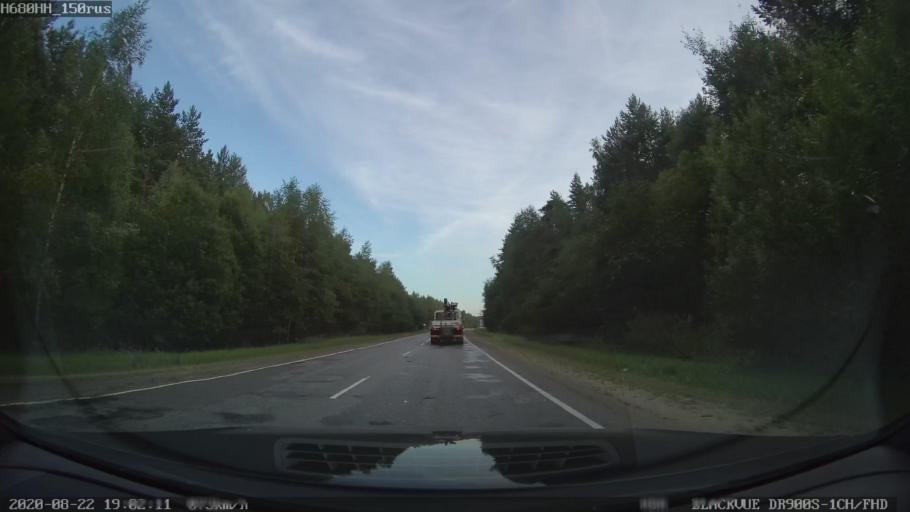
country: RU
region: Tverskaya
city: Sakharovo
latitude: 57.1113
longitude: 36.1190
